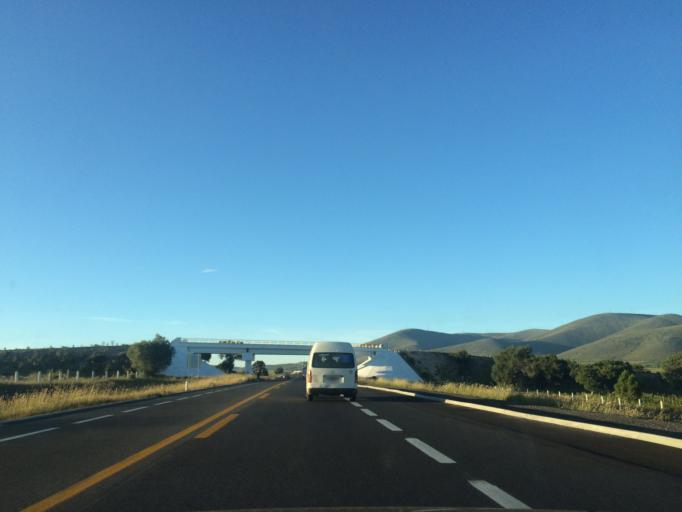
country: MX
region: Puebla
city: Cuacnopalan
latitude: 18.7609
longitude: -97.4826
